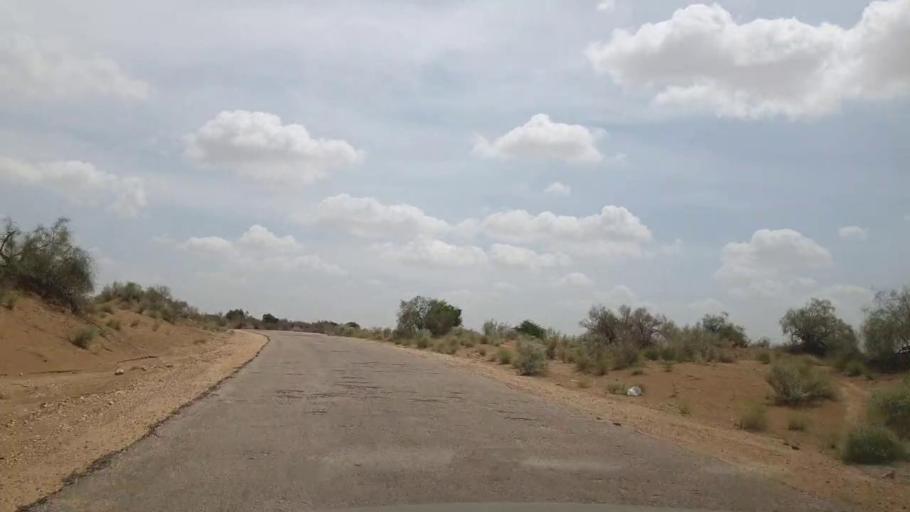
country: PK
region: Sindh
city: Kot Diji
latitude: 27.1446
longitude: 69.2247
